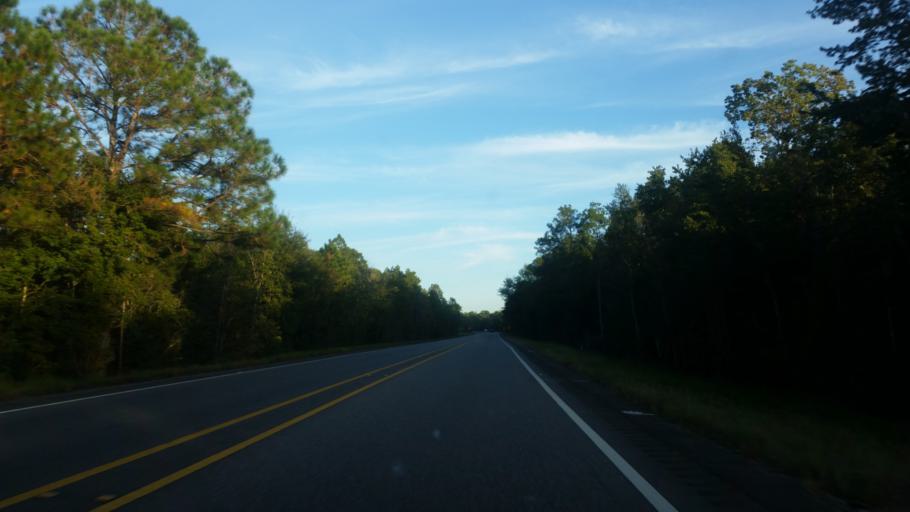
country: US
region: Alabama
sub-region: Mobile County
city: Grand Bay
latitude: 30.4698
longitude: -88.3893
